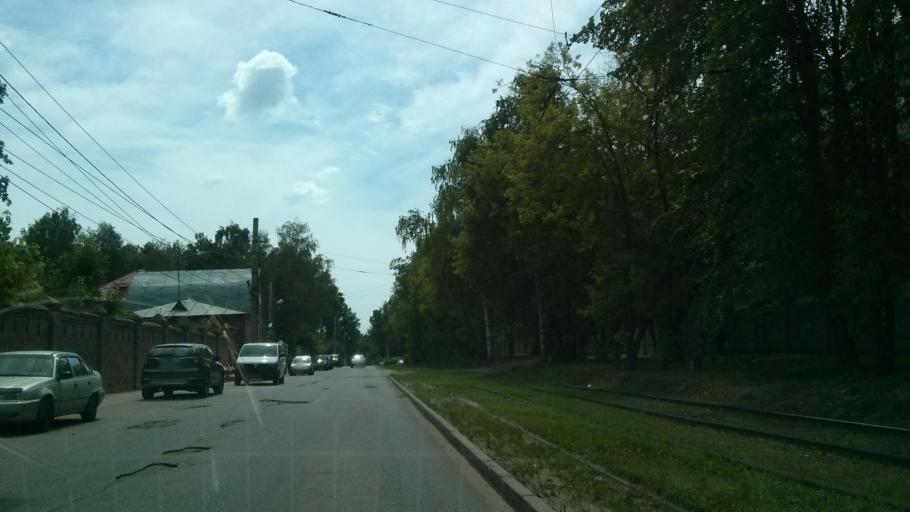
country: RU
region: Nizjnij Novgorod
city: Nizhniy Novgorod
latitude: 56.3005
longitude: 43.9915
